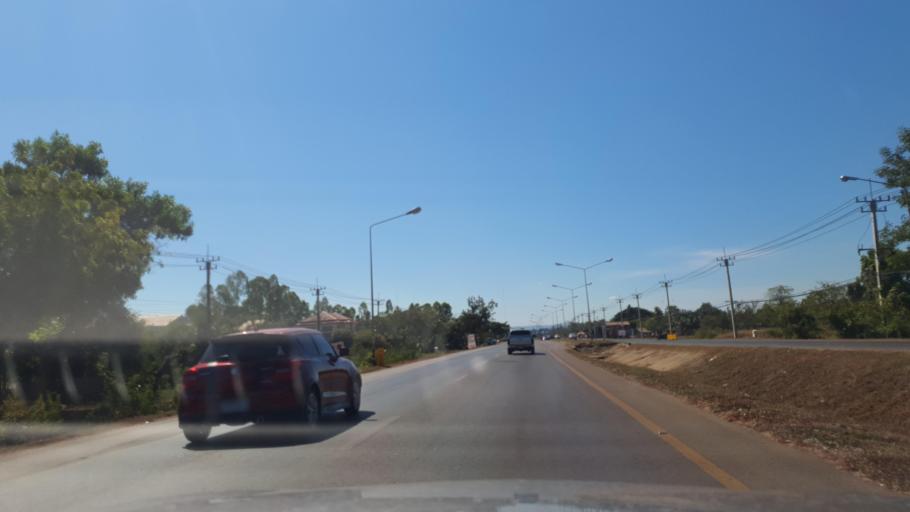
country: TH
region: Sakon Nakhon
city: Sakon Nakhon
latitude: 17.2181
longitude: 104.1043
